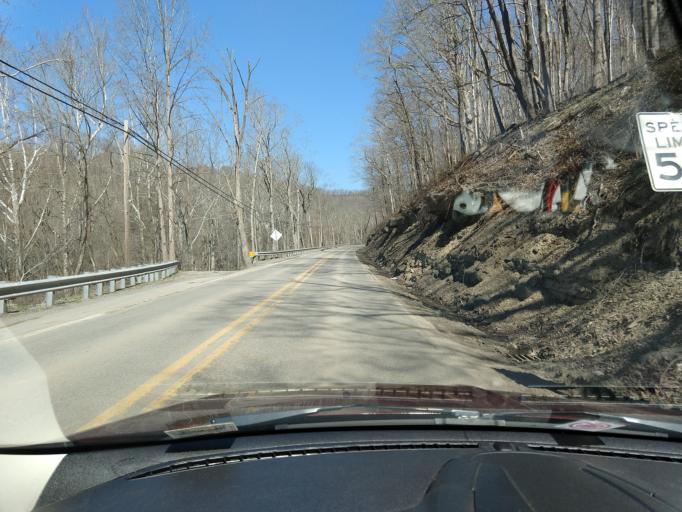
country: US
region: West Virginia
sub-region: Braxton County
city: Sutton
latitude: 38.6708
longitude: -80.7165
